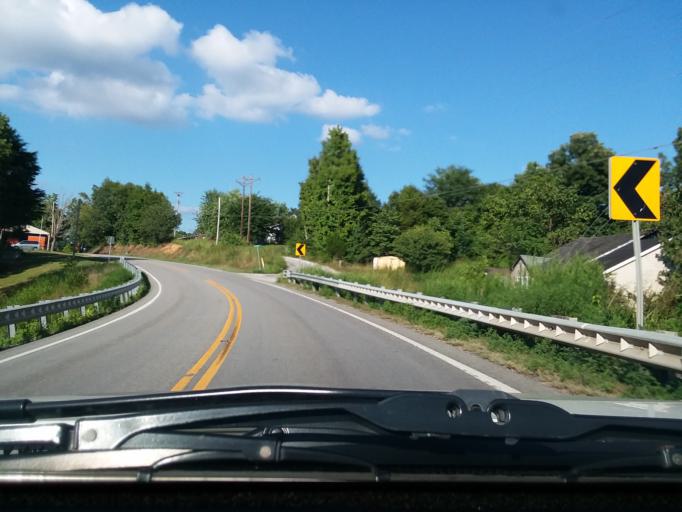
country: US
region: Tennessee
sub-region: Clay County
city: Celina
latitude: 36.5885
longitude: -85.6085
